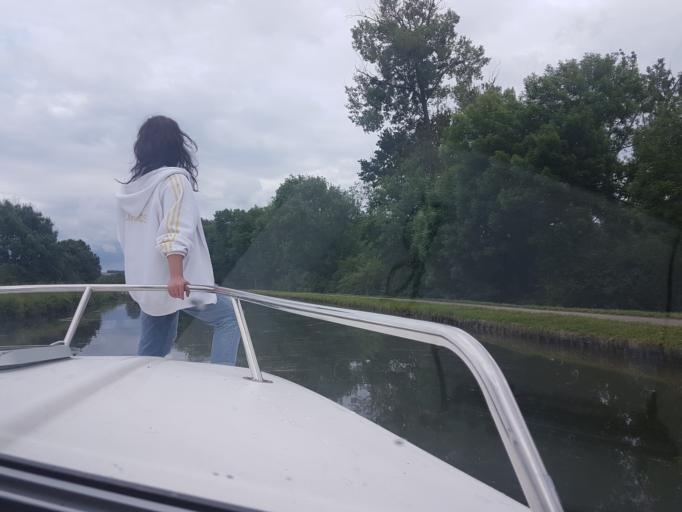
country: FR
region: Bourgogne
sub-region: Departement de l'Yonne
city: Saint-Bris-le-Vineux
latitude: 47.6968
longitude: 3.6437
